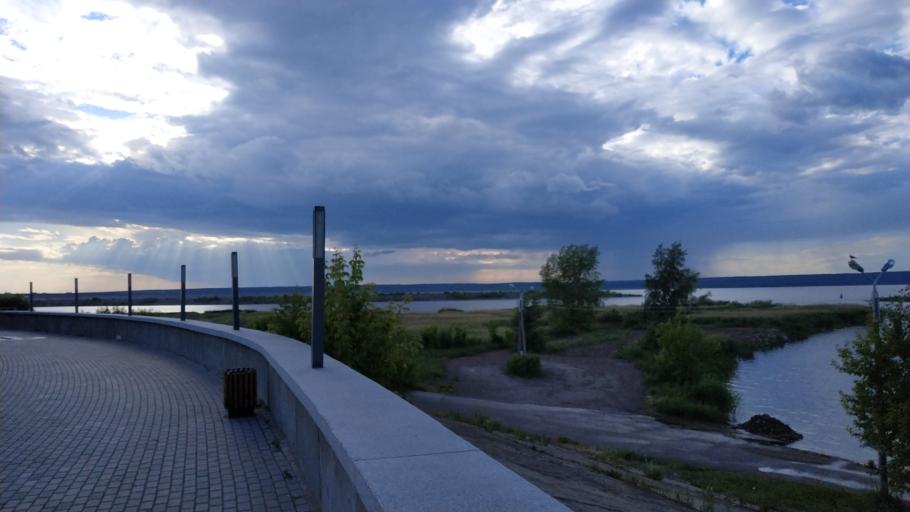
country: RU
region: Tatarstan
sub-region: Tukayevskiy Rayon
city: Naberezhnyye Chelny
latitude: 55.7030
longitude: 52.3119
